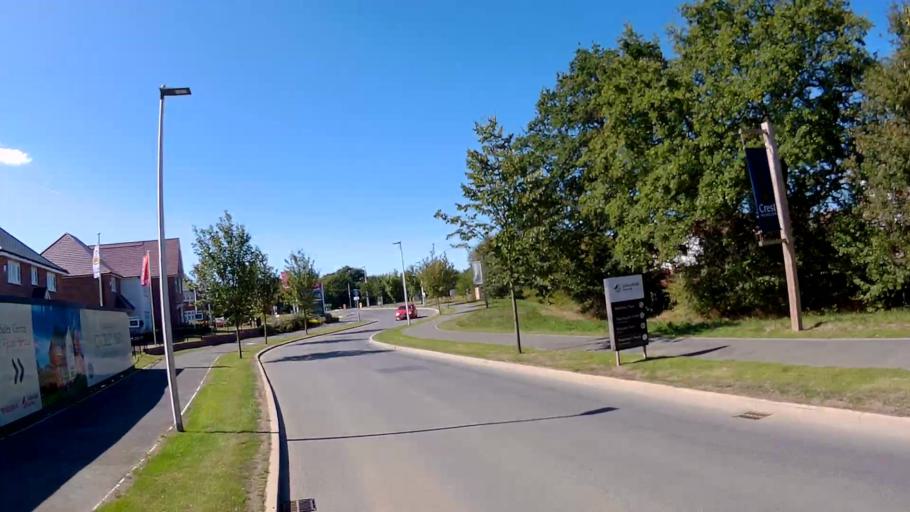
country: GB
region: England
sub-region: Hampshire
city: Eversley
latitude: 51.3786
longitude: -0.9028
